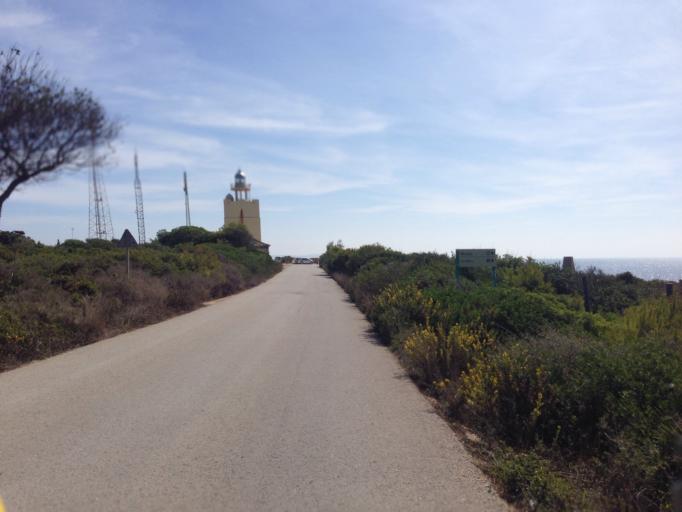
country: ES
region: Andalusia
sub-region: Provincia de Cadiz
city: Conil de la Frontera
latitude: 36.2964
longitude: -6.1414
